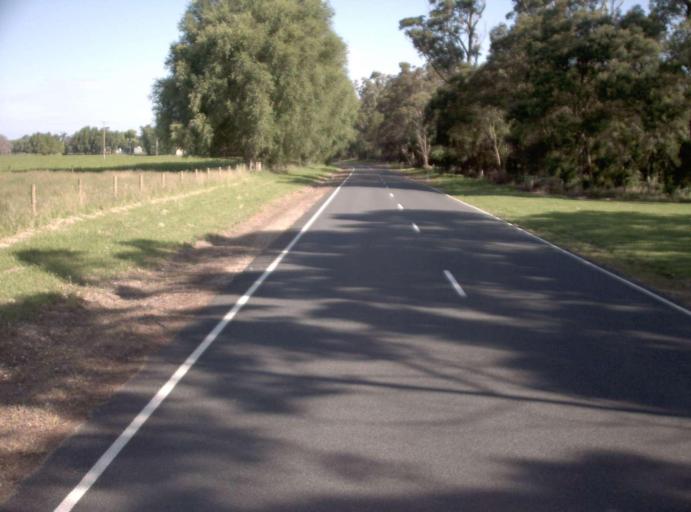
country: AU
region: Victoria
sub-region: East Gippsland
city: Lakes Entrance
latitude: -37.7478
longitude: 148.5172
